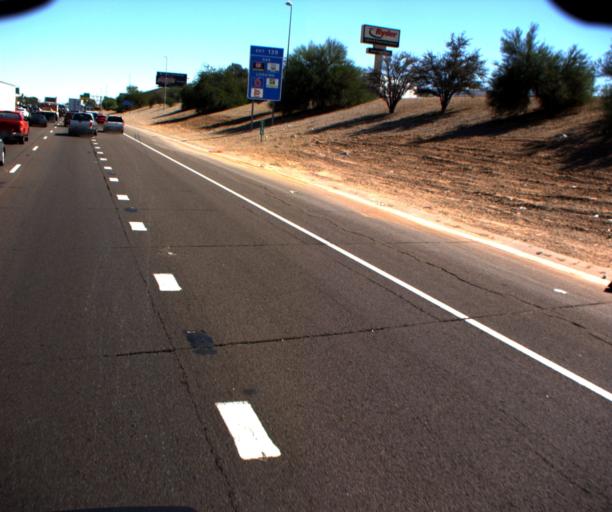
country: US
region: Arizona
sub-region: Maricopa County
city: Glendale
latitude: 33.4627
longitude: -112.1810
